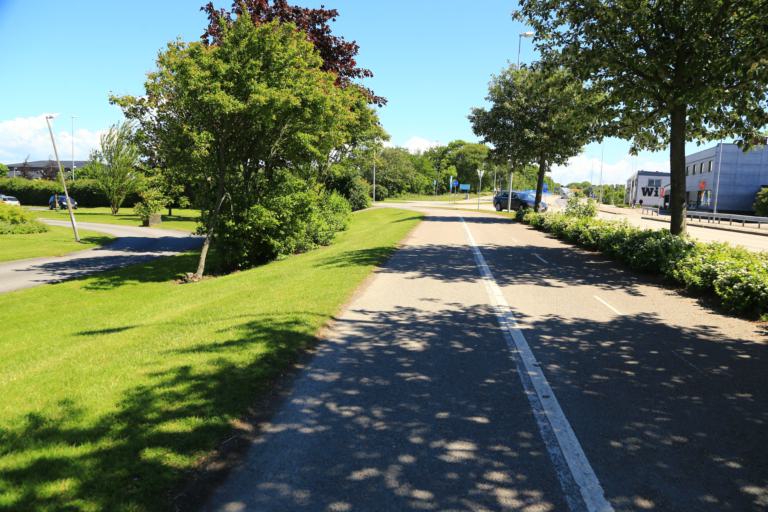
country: SE
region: Halland
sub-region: Varbergs Kommun
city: Varberg
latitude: 57.1028
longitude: 12.2661
